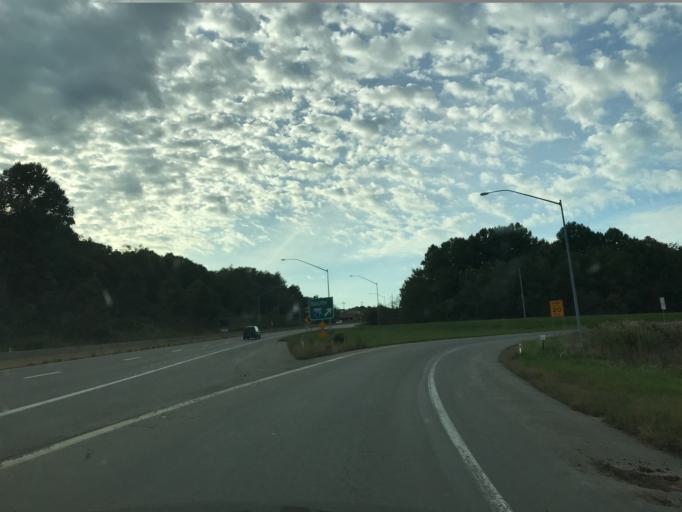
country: US
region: Pennsylvania
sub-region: Crawford County
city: Meadville
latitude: 41.6230
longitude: -80.1841
